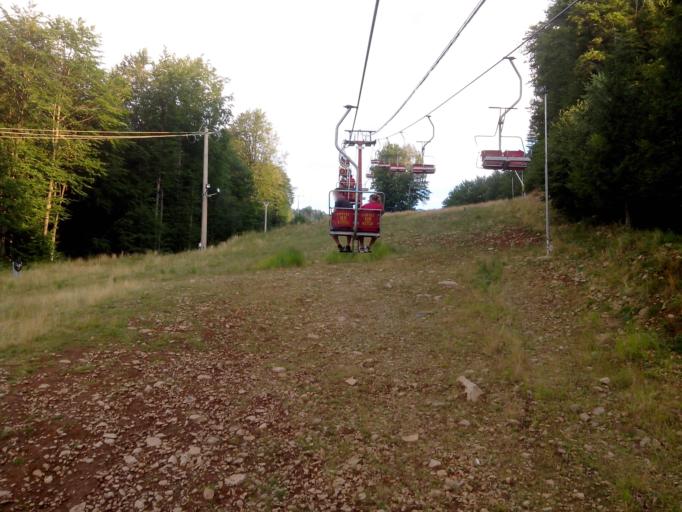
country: RO
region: Maramures
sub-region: Comuna Sisesti
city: Surdesti
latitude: 47.6680
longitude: 23.7819
